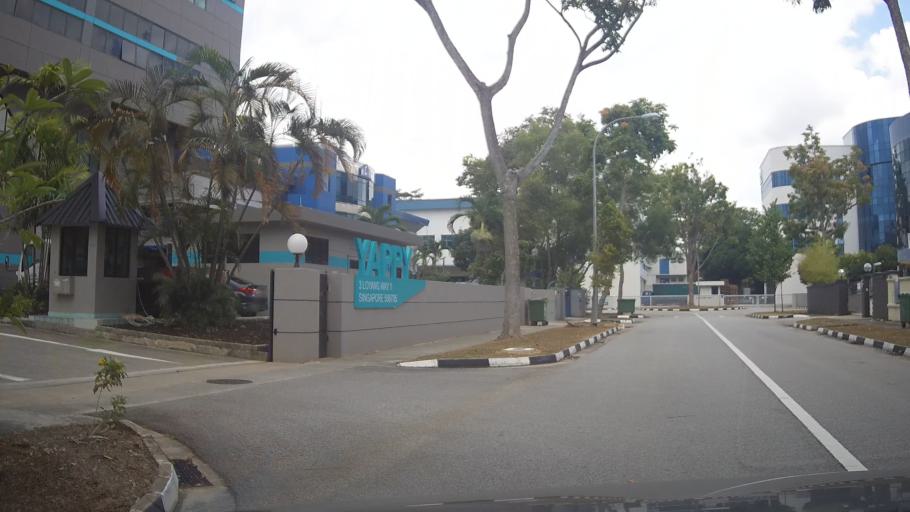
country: MY
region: Johor
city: Kampung Pasir Gudang Baru
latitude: 1.3749
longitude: 103.9722
